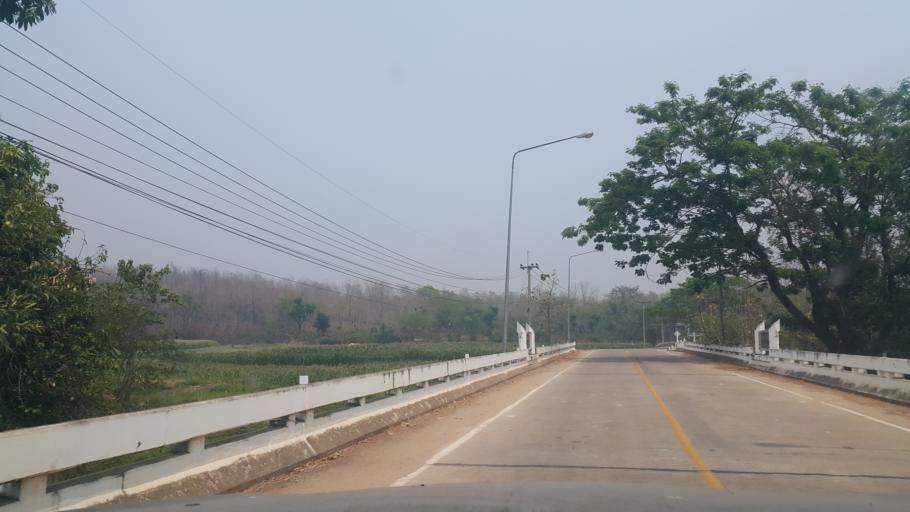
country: TH
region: Lampang
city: Soem Ngam
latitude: 18.1669
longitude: 99.1769
